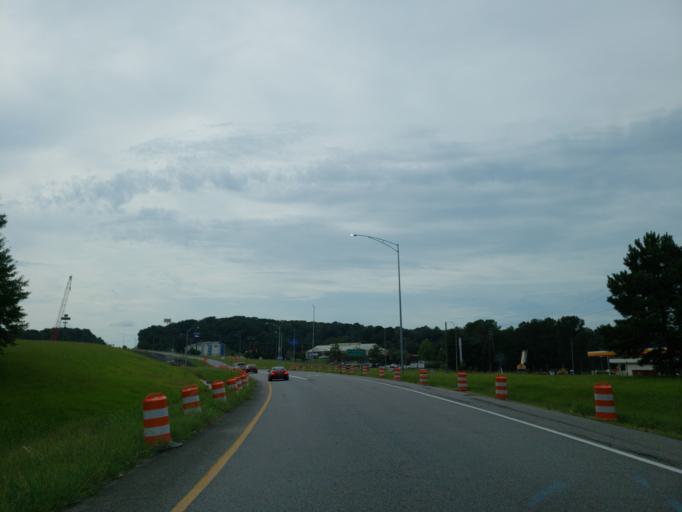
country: US
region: Alabama
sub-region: Tuscaloosa County
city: Holt
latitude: 33.1743
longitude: -87.4714
